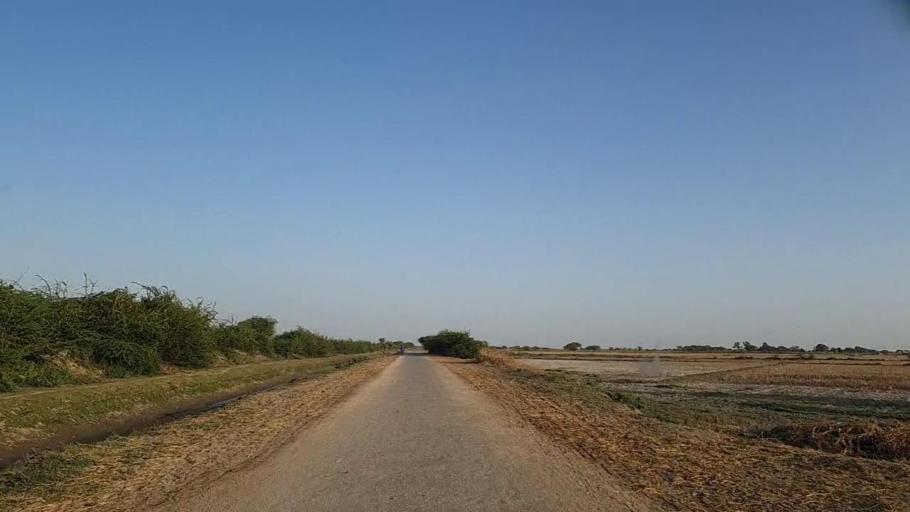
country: PK
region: Sindh
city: Jati
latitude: 24.4124
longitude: 68.3462
